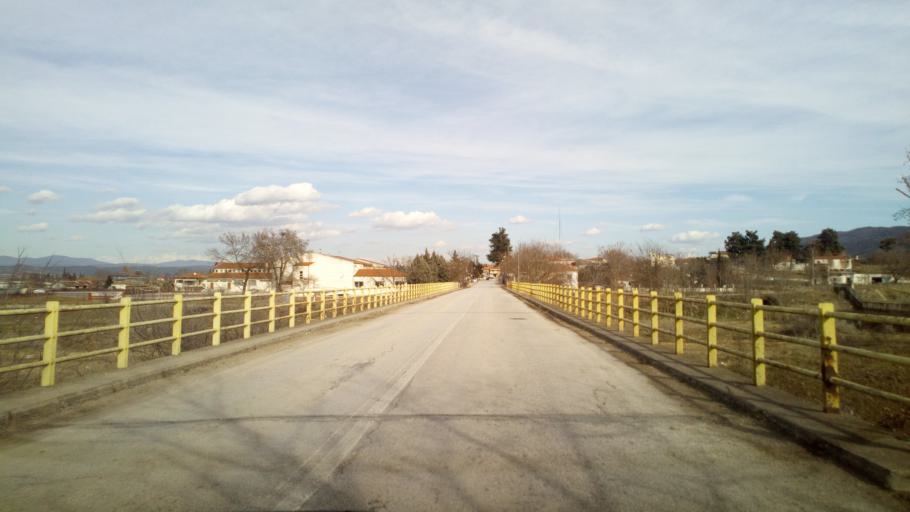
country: GR
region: Central Macedonia
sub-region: Nomos Thessalonikis
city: Gerakarou
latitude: 40.6335
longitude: 23.2419
